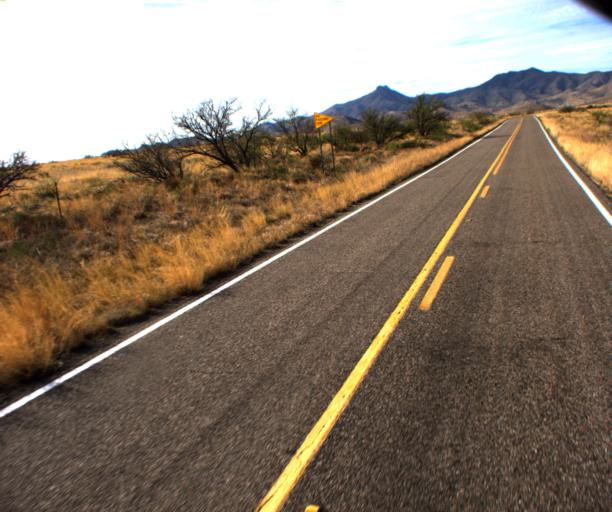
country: US
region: Arizona
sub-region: Cochise County
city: Willcox
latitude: 32.1205
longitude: -109.5551
